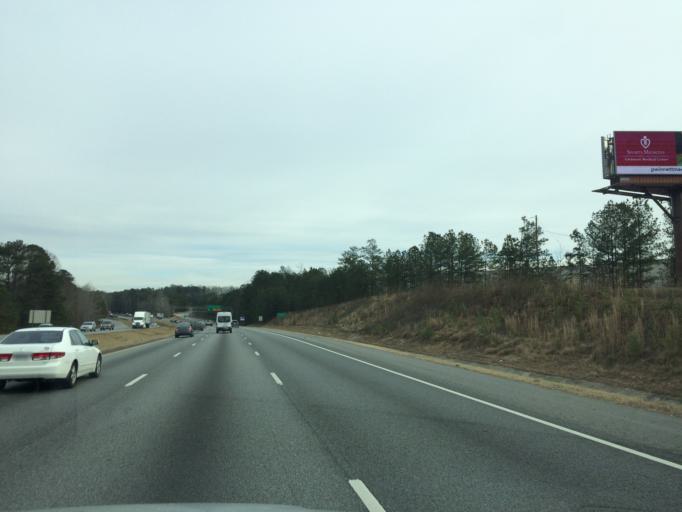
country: US
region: Georgia
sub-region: Gwinnett County
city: Lawrenceville
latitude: 33.9588
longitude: -84.0443
